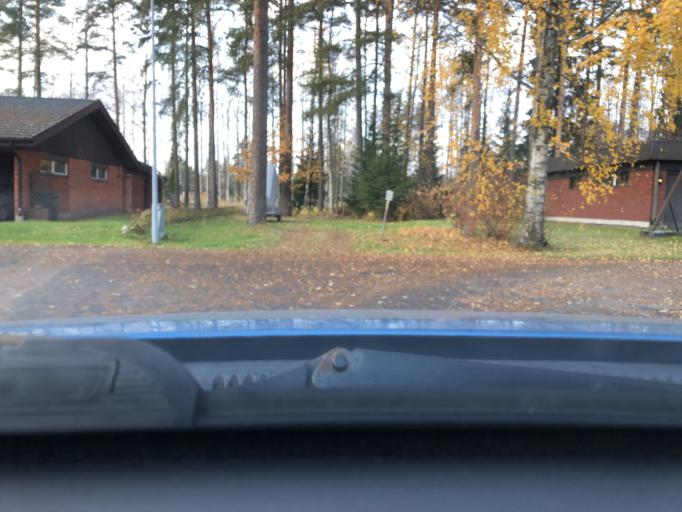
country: FI
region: Pirkanmaa
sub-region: Tampere
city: Kangasala
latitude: 61.4678
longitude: 24.0270
